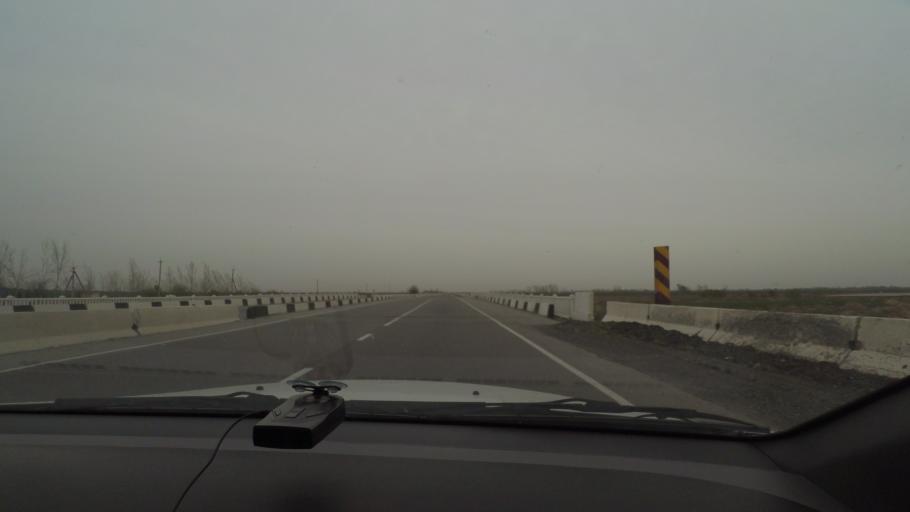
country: UZ
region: Jizzax
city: Dustlik
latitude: 40.4196
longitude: 68.2123
